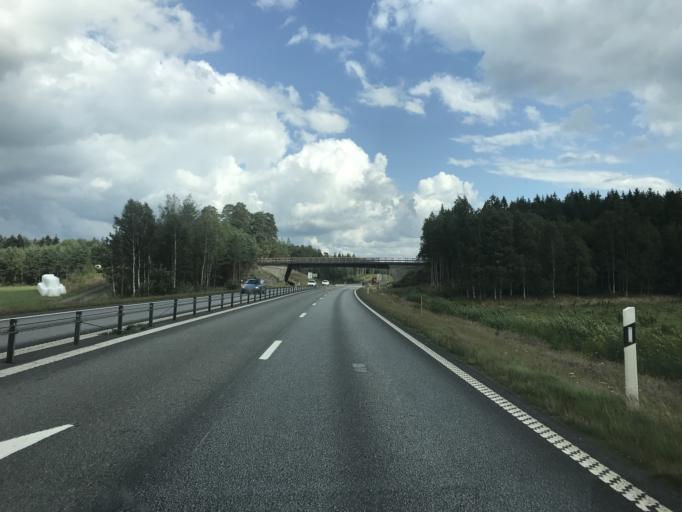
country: SE
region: Skane
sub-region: Hassleholms Kommun
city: Hassleholm
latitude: 56.1831
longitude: 13.7681
